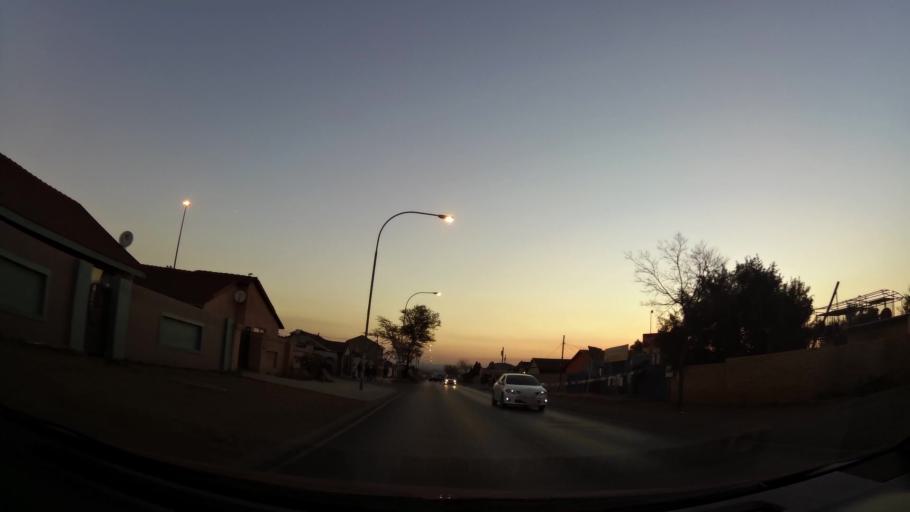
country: ZA
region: Gauteng
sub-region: City of Johannesburg Metropolitan Municipality
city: Soweto
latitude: -26.2341
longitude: 27.8290
